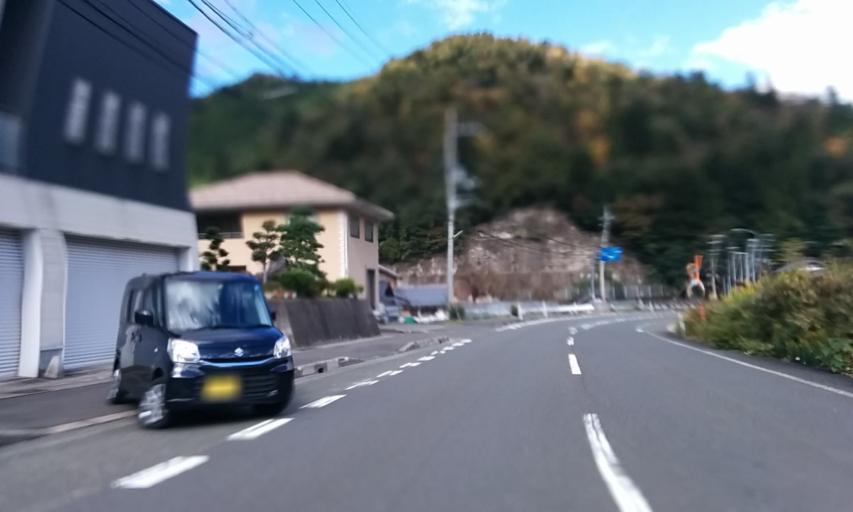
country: JP
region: Fukui
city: Obama
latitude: 35.3987
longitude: 135.6104
